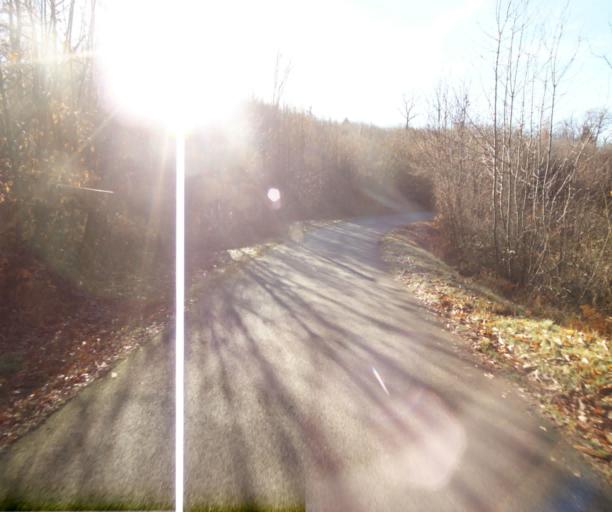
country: FR
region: Limousin
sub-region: Departement de la Correze
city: Sainte-Fortunade
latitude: 45.2103
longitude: 1.7879
